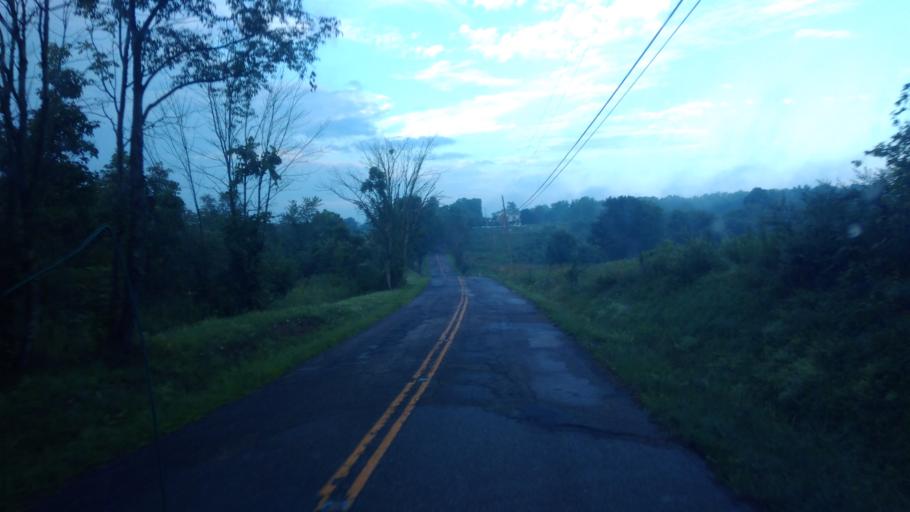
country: US
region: Ohio
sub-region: Guernsey County
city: Byesville
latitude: 40.0277
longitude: -81.4568
